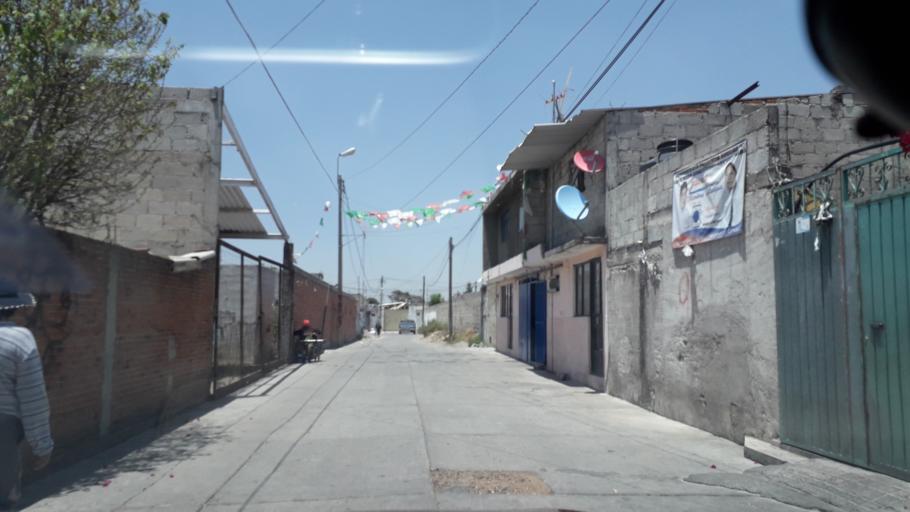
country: MX
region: Puebla
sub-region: Puebla
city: Santa Maria Xonacatepec
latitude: 19.0865
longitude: -98.1064
